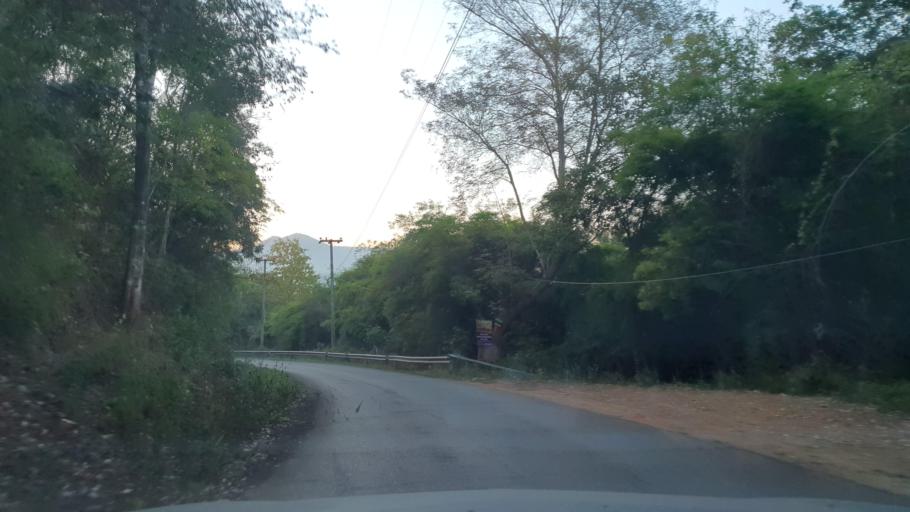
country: TH
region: Chiang Mai
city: Mae Wang
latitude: 18.6903
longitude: 98.8151
